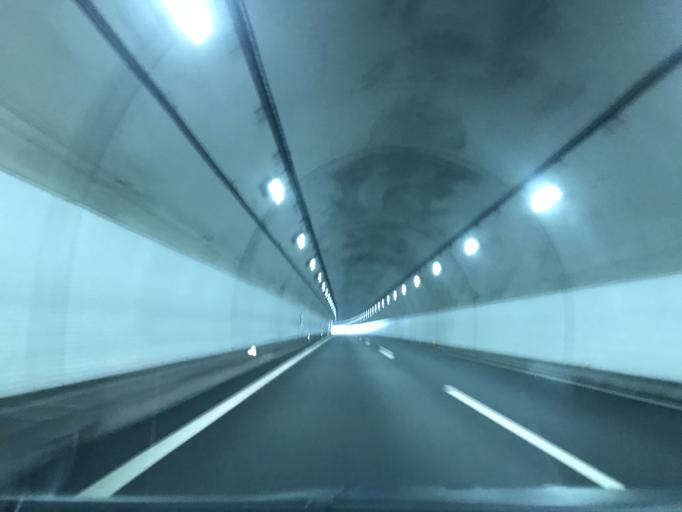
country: JP
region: Fukuoka
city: Kanda
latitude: 33.8099
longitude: 130.9134
